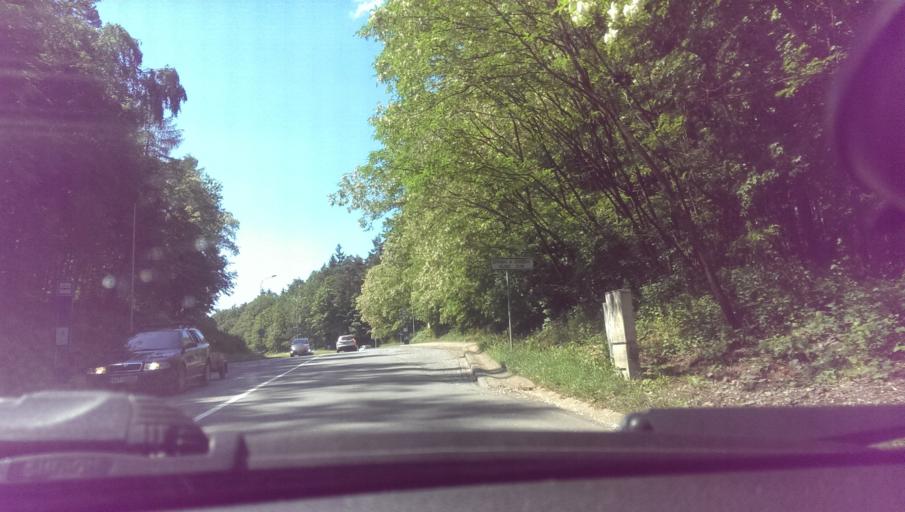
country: CZ
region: Zlin
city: Breznice
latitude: 49.2025
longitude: 17.6603
